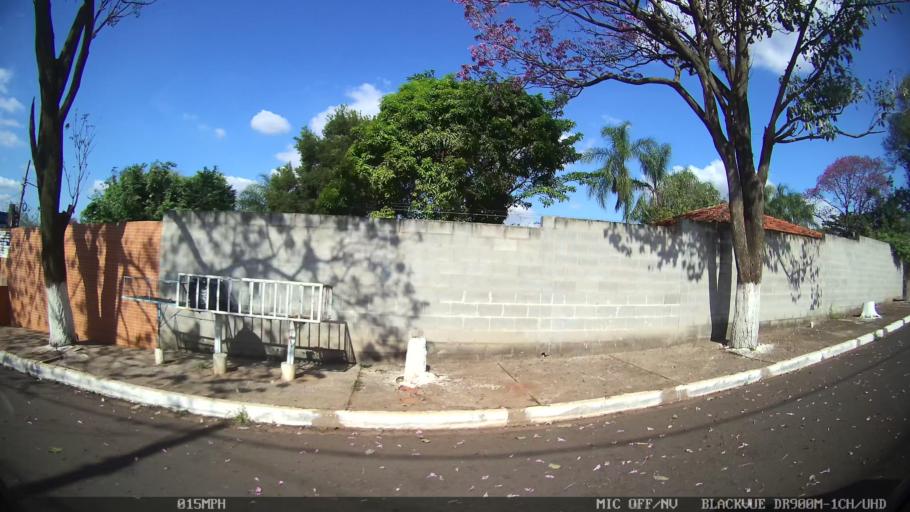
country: BR
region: Sao Paulo
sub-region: Sumare
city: Sumare
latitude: -22.8350
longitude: -47.2616
